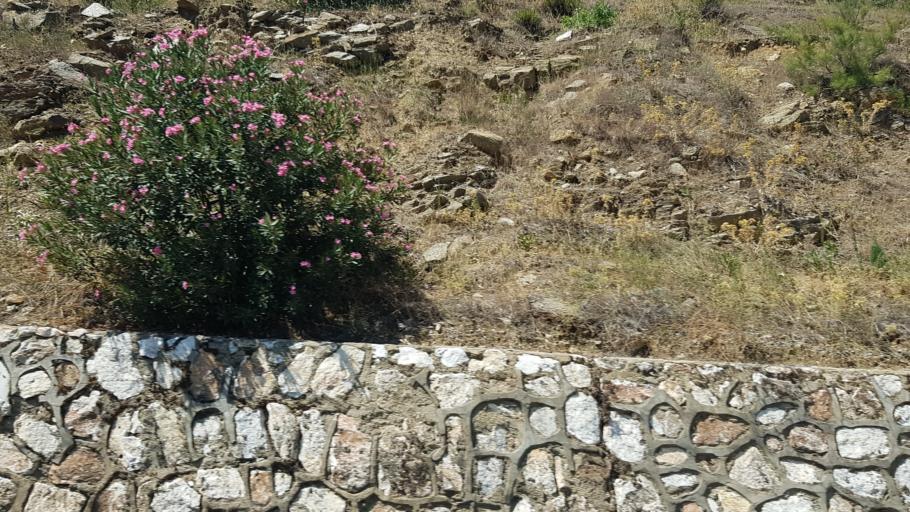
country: TR
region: Aydin
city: Akcaova
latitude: 37.5068
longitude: 28.1023
